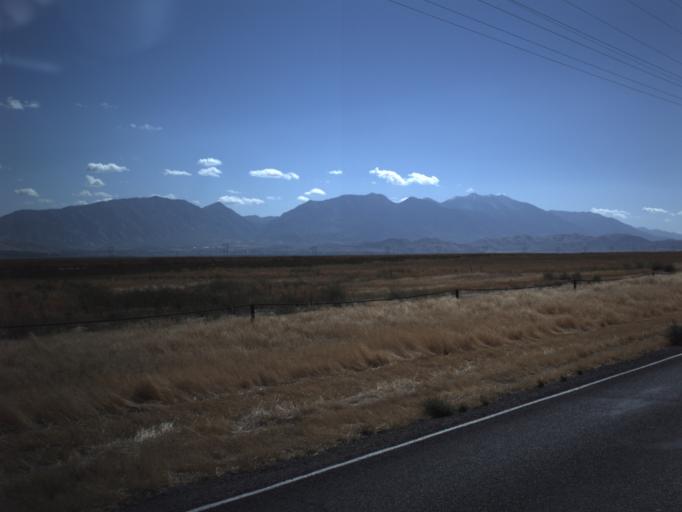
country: US
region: Utah
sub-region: Utah County
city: Genola
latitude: 40.0914
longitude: -111.9589
